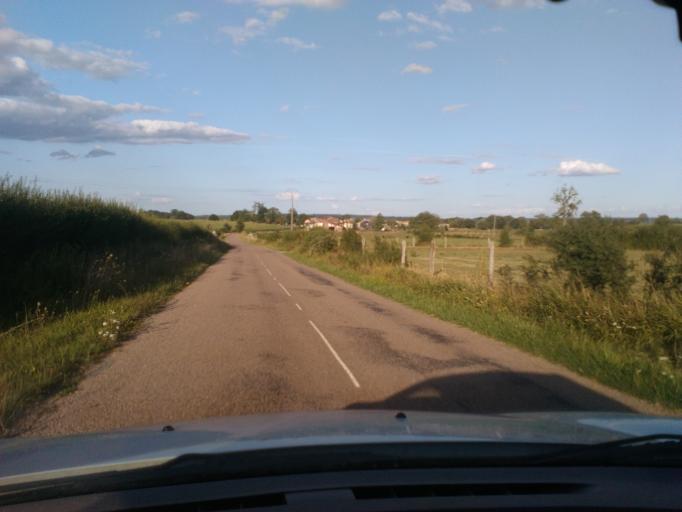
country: FR
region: Lorraine
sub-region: Departement des Vosges
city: Mirecourt
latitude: 48.3499
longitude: 6.0518
